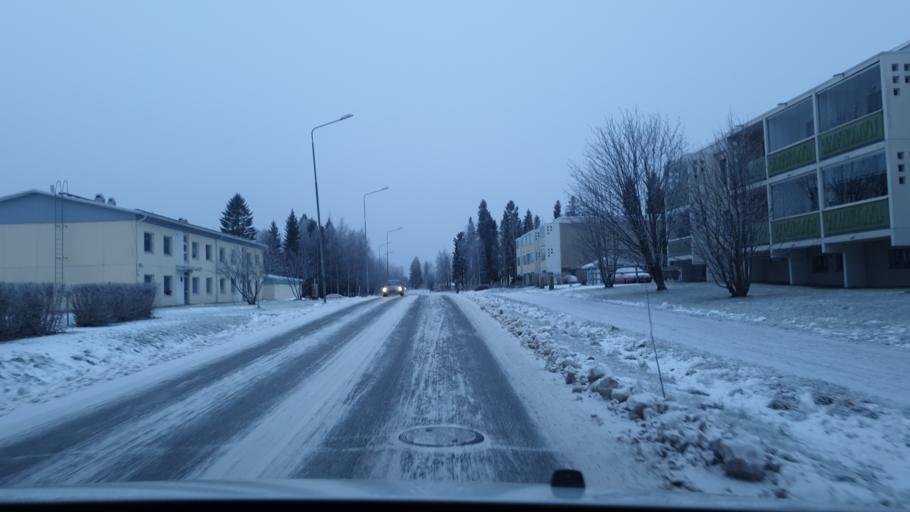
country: FI
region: Lapland
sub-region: Kemi-Tornio
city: Kemi
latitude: 65.7339
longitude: 24.6095
